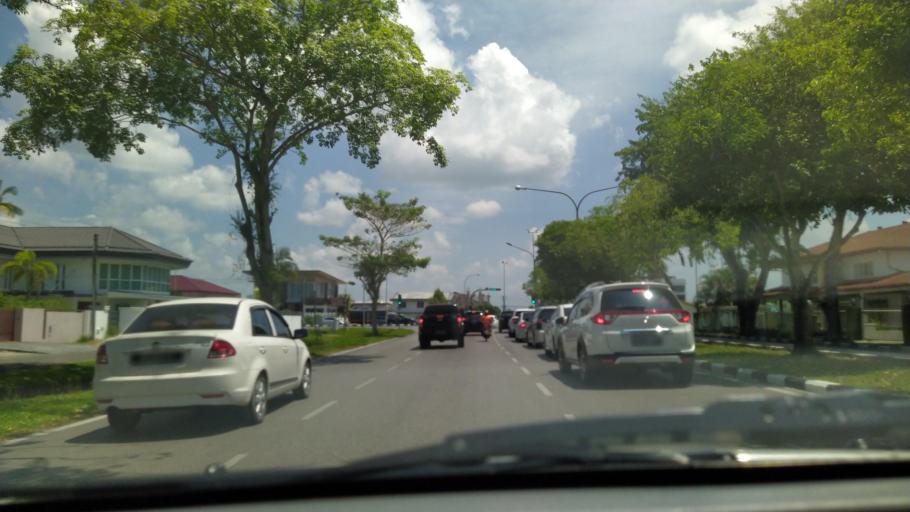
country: MY
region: Sarawak
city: Sibu
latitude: 2.3054
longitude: 111.8290
